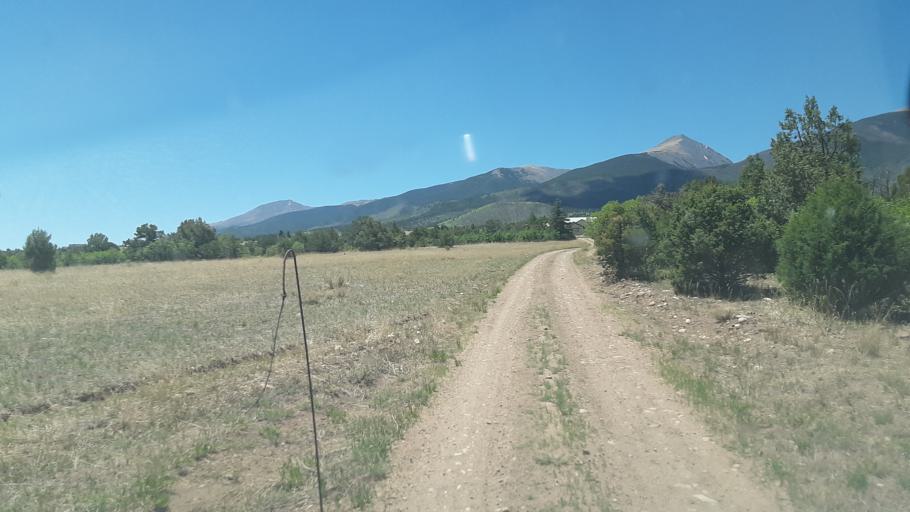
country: US
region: Colorado
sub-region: Custer County
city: Westcliffe
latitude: 38.3026
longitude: -105.6781
